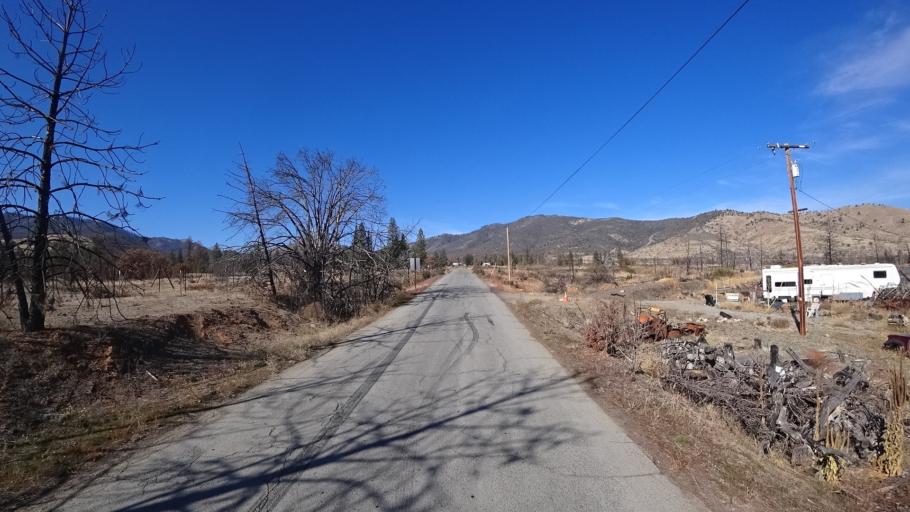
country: US
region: California
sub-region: Siskiyou County
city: Yreka
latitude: 41.7646
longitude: -122.6273
